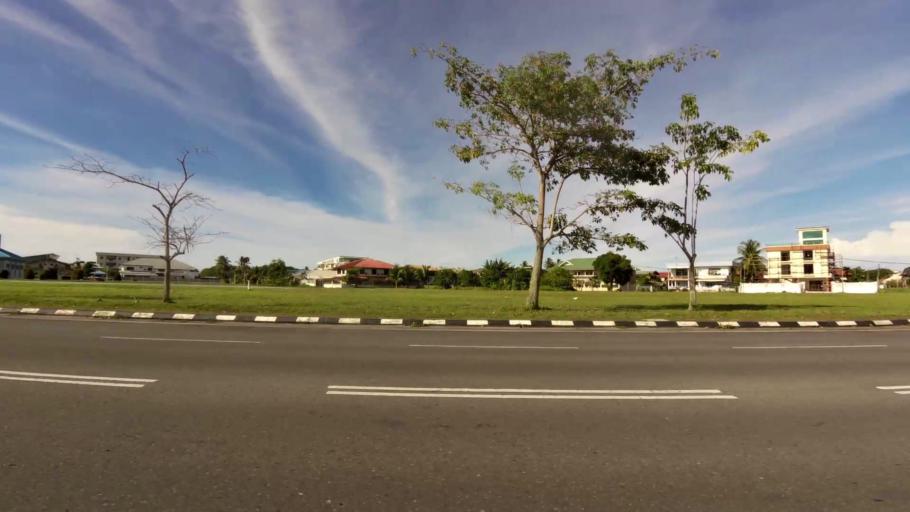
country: BN
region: Belait
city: Kuala Belait
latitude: 4.5794
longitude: 114.1949
